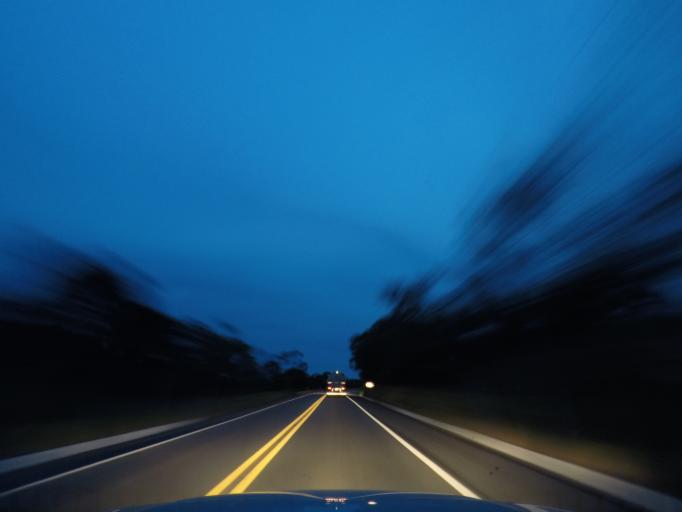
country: BR
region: Bahia
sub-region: Andarai
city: Vera Cruz
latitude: -12.4956
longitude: -41.3280
